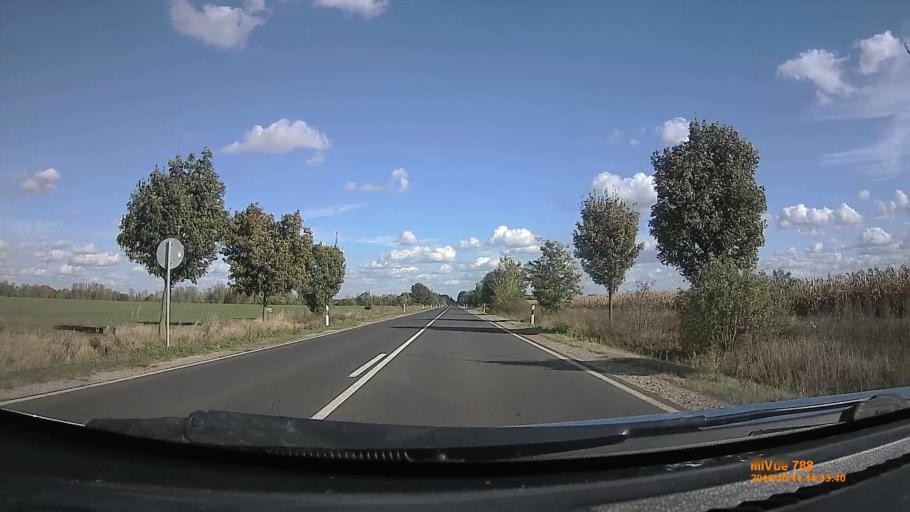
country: HU
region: Hajdu-Bihar
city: Ebes
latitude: 47.5617
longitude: 21.4604
